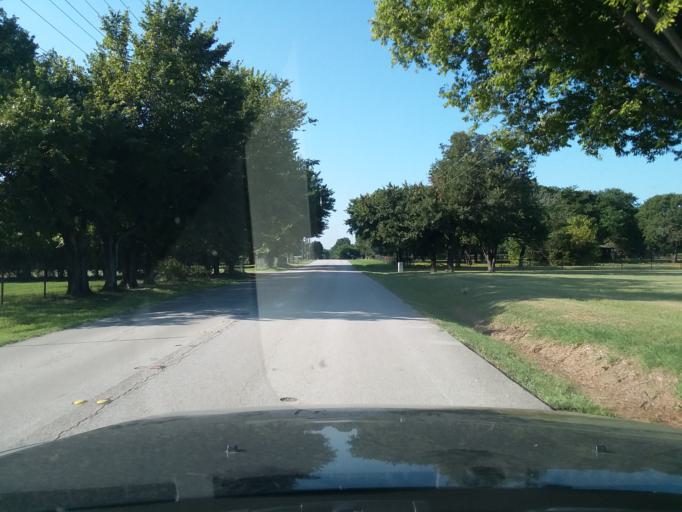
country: US
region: Texas
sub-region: Denton County
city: Copper Canyon
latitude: 33.1100
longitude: -97.0877
